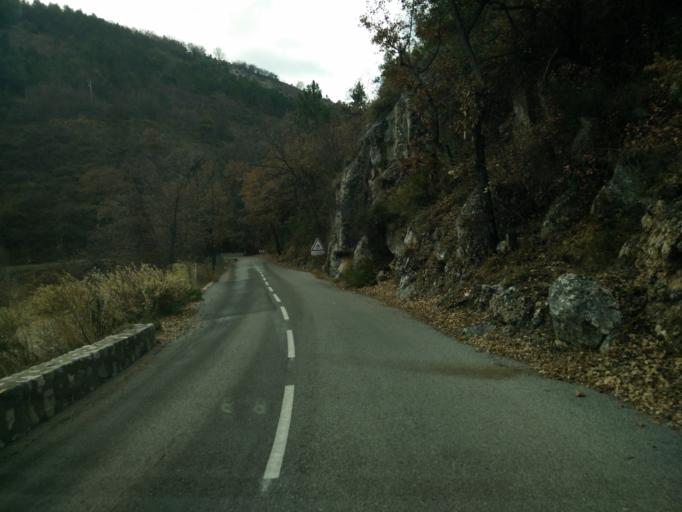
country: FR
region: Provence-Alpes-Cote d'Azur
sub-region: Departement des Alpes-Maritimes
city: Le Broc
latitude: 43.8188
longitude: 7.1598
